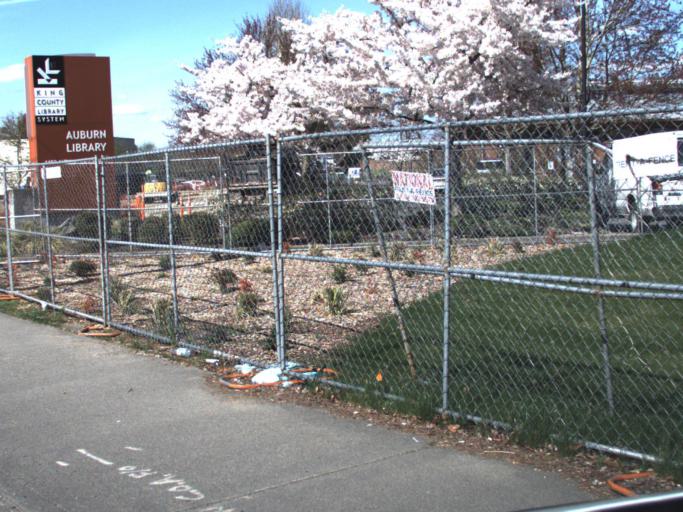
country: US
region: Washington
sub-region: King County
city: Auburn
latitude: 47.2980
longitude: -122.2186
